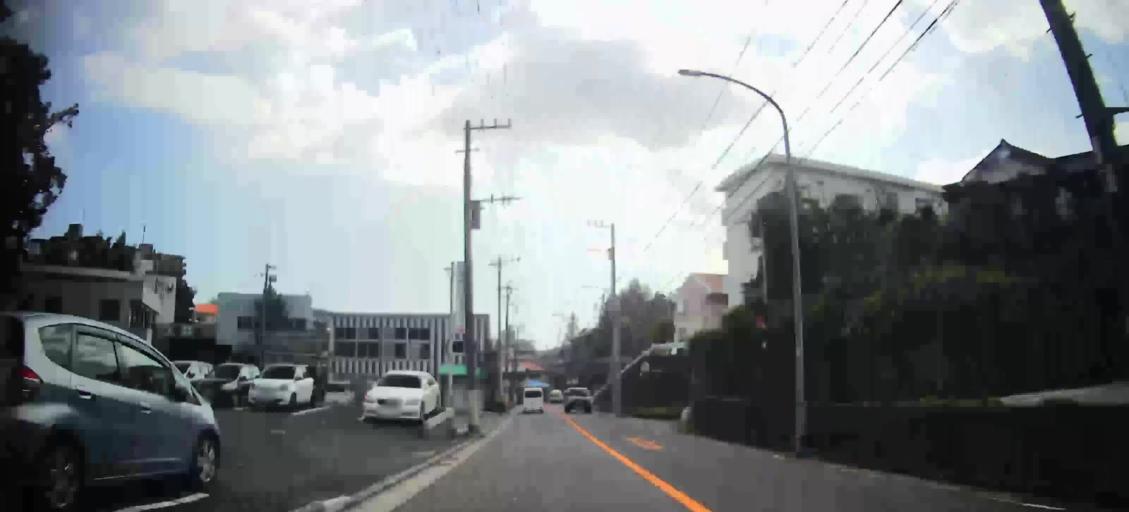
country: JP
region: Kanagawa
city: Yokohama
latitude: 35.4792
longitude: 139.5768
